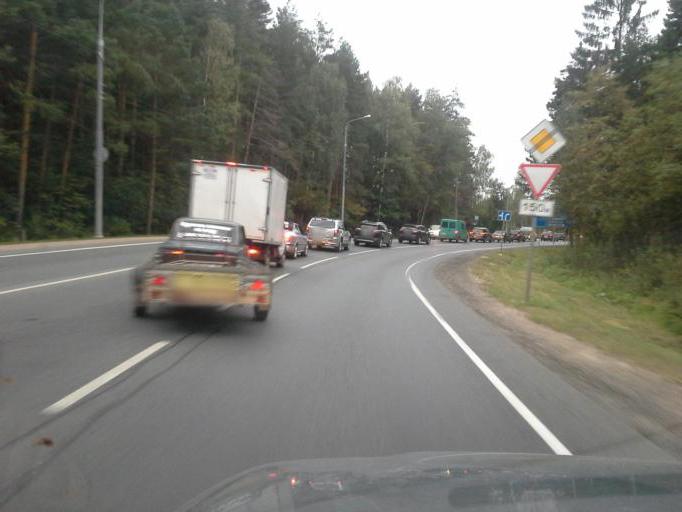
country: RU
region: Moskovskaya
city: Zhavoronki
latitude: 55.6576
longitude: 37.0974
